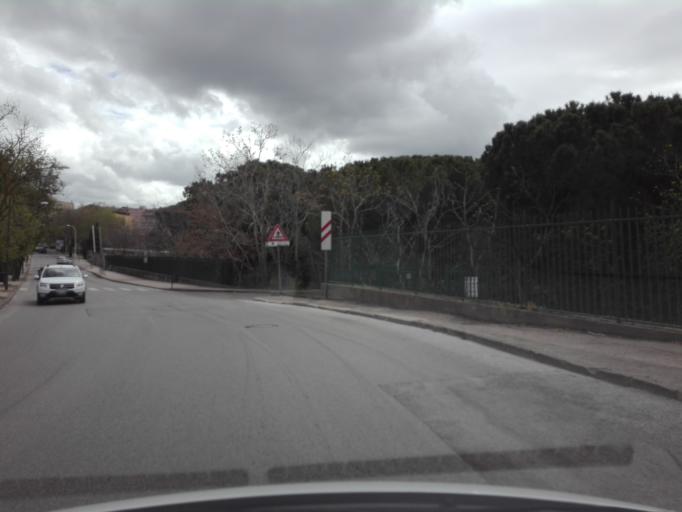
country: IT
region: Sardinia
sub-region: Provincia di Sassari
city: Sassari
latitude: 40.7389
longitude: 8.5587
